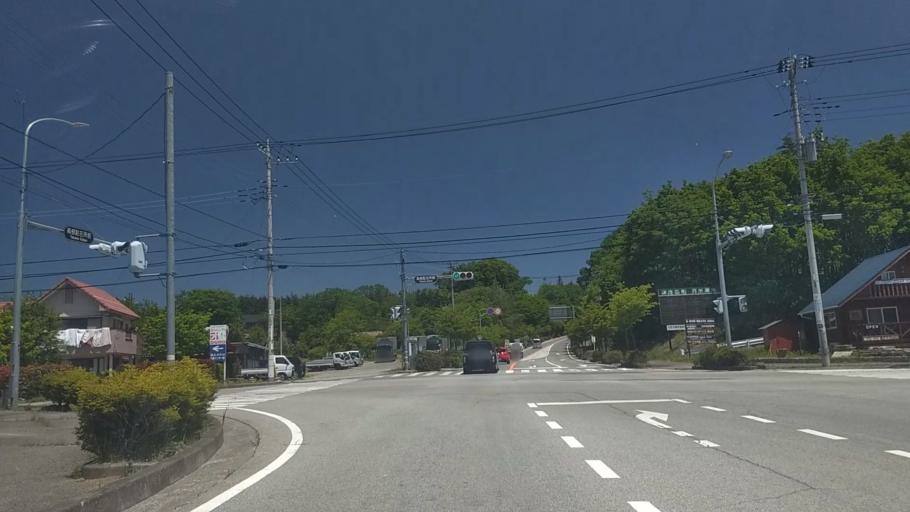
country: JP
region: Yamanashi
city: Nirasaki
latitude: 35.8358
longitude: 138.4300
